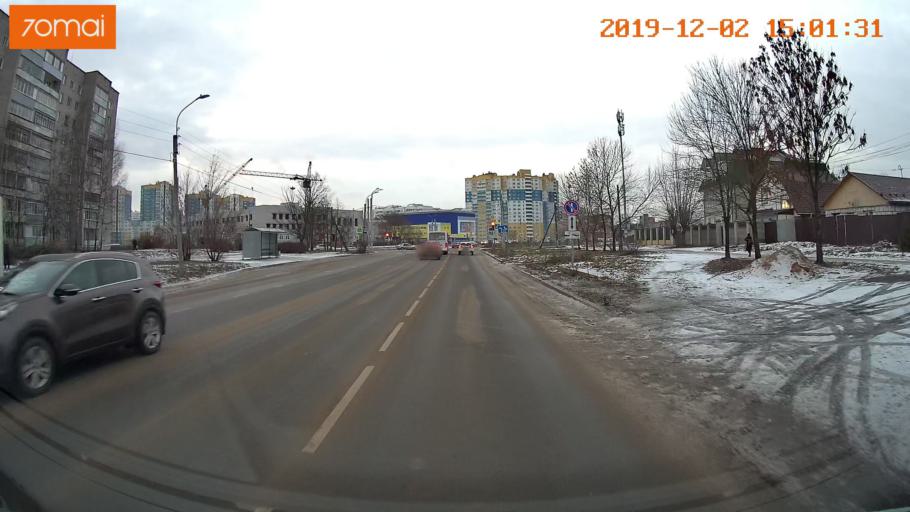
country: RU
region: Ivanovo
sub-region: Gorod Ivanovo
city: Ivanovo
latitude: 56.9719
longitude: 40.9947
